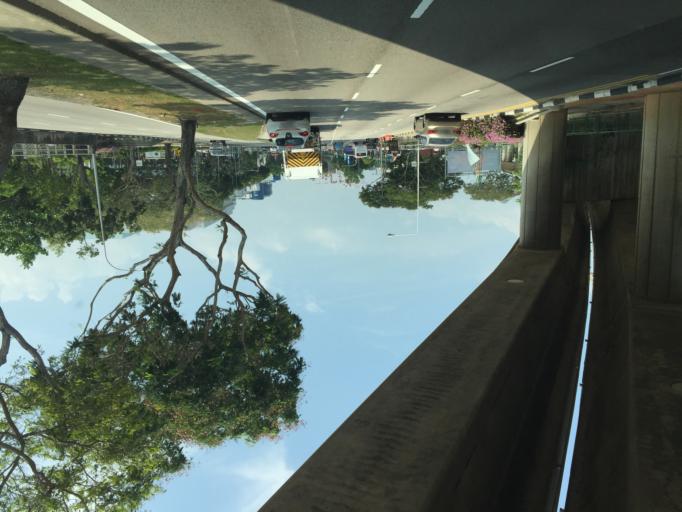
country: SG
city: Singapore
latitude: 1.3333
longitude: 103.9561
